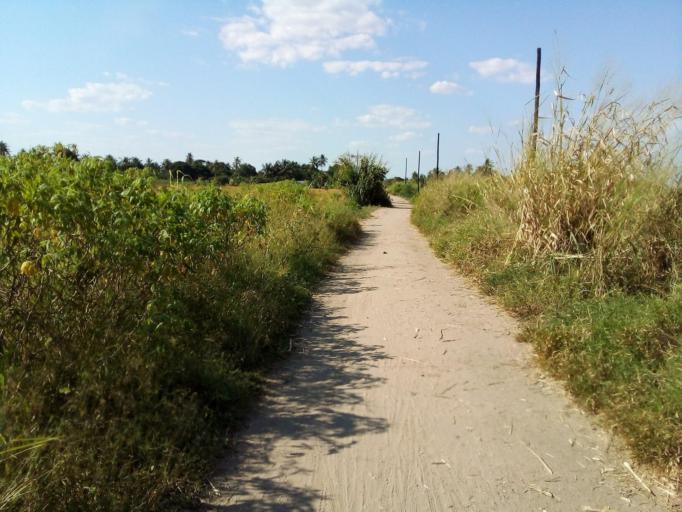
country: MZ
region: Zambezia
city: Quelimane
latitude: -17.5955
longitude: 36.8301
